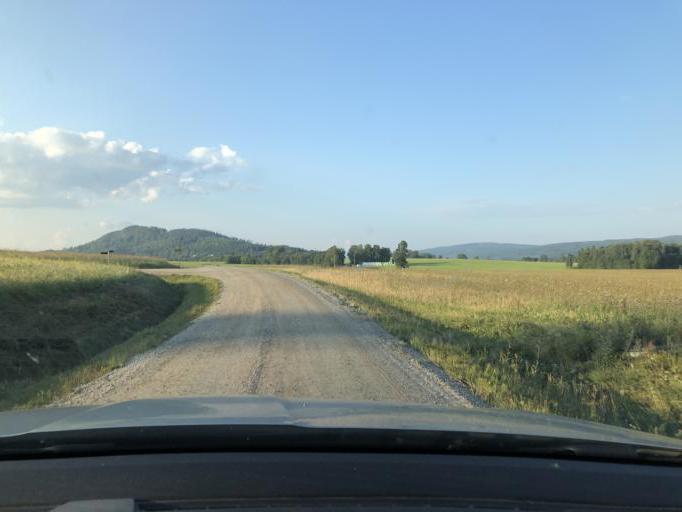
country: SE
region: Vaesternorrland
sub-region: Kramfors Kommun
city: Bollstabruk
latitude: 63.0696
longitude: 17.7341
